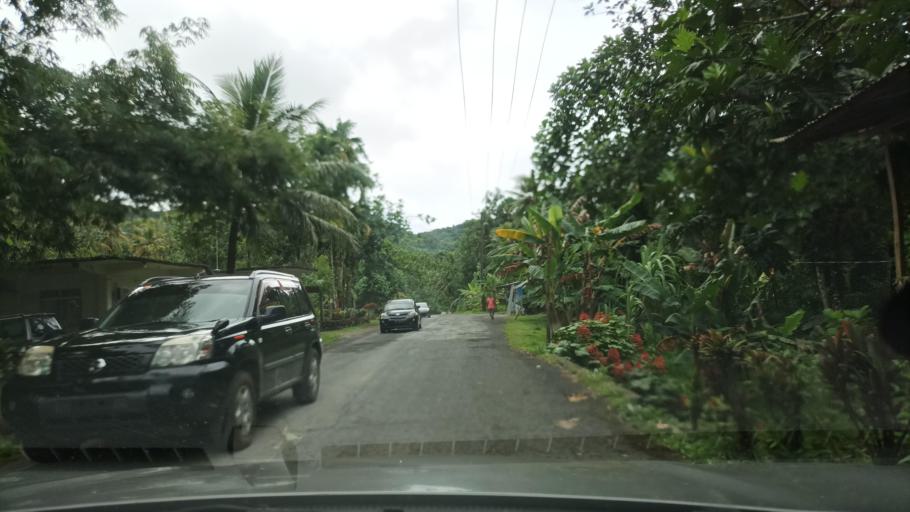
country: FM
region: Pohnpei
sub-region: Kolonia Municipality
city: Kolonia
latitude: 6.9420
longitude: 158.2757
